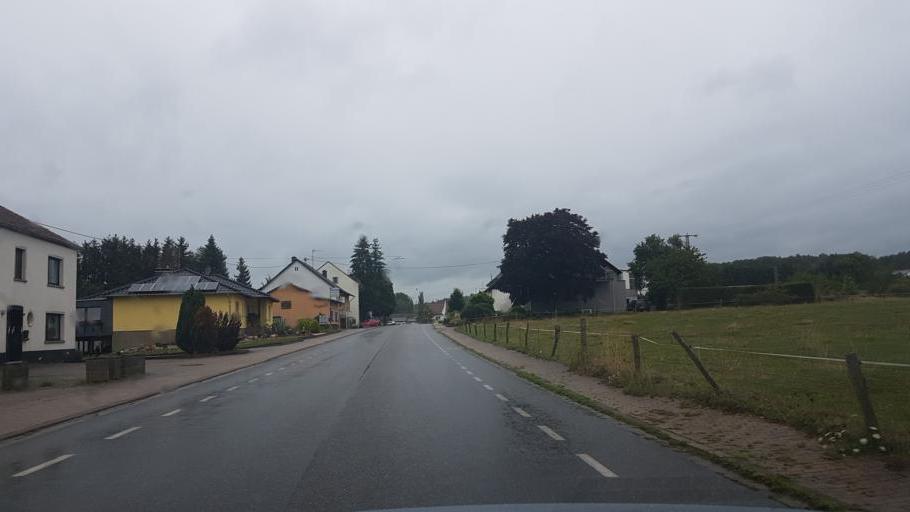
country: DE
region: Saarland
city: Losheim
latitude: 49.5041
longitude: 6.7839
